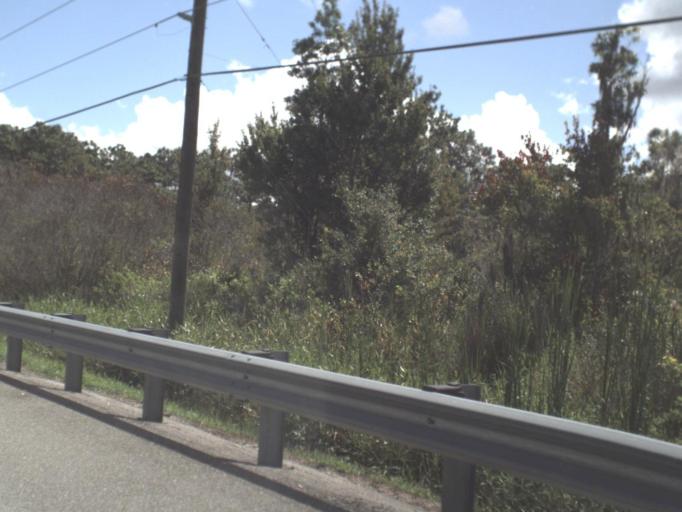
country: US
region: Florida
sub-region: Sarasota County
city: Lake Sarasota
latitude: 27.3873
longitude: -82.2783
